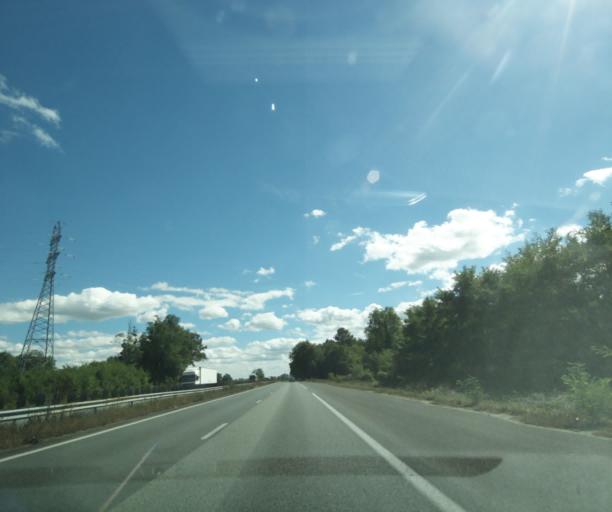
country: FR
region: Aquitaine
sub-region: Departement de la Gironde
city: Illats
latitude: 44.5895
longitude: -0.3525
